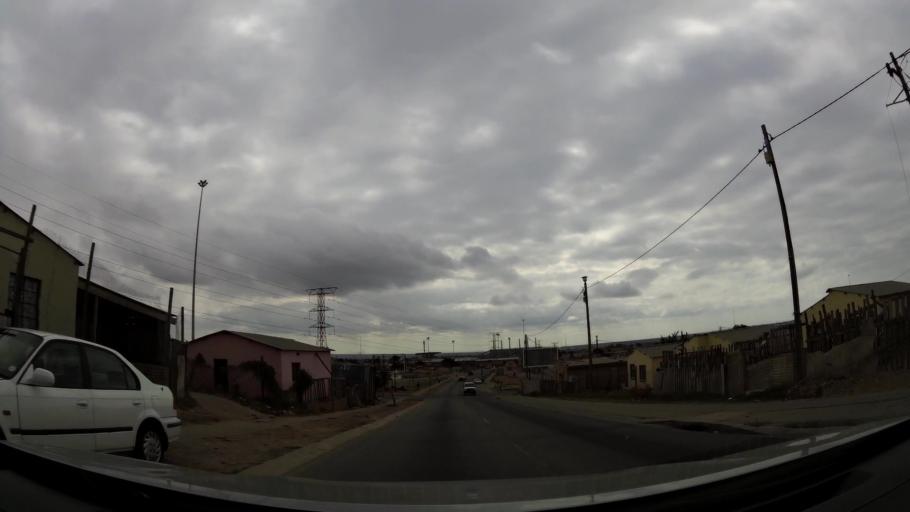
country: ZA
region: Eastern Cape
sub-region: Nelson Mandela Bay Metropolitan Municipality
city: Port Elizabeth
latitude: -33.8897
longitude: 25.5951
